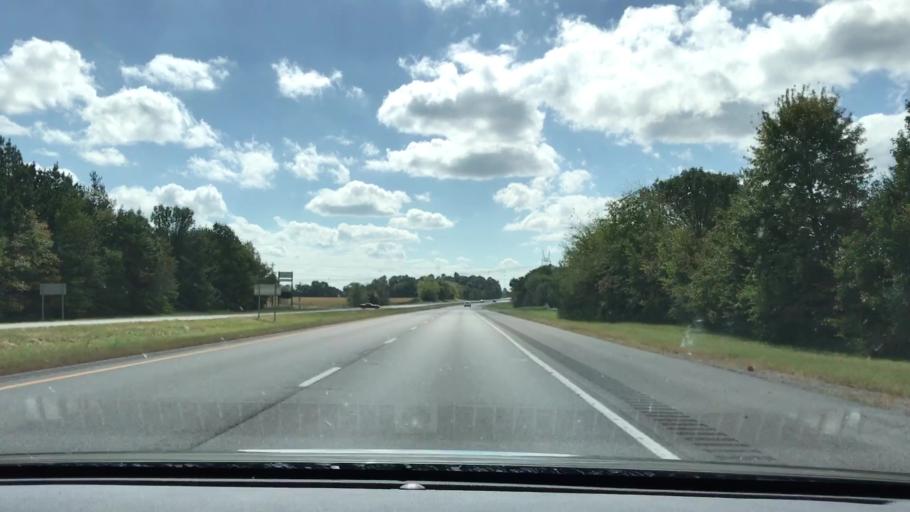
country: US
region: Kentucky
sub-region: McCracken County
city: Reidland
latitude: 37.0059
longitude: -88.5077
